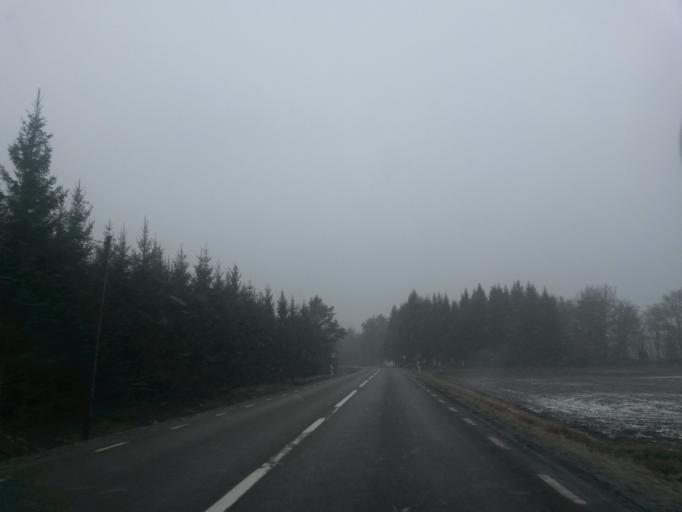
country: SE
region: Vaestra Goetaland
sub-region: Alingsas Kommun
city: Sollebrunn
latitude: 58.2116
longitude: 12.4331
